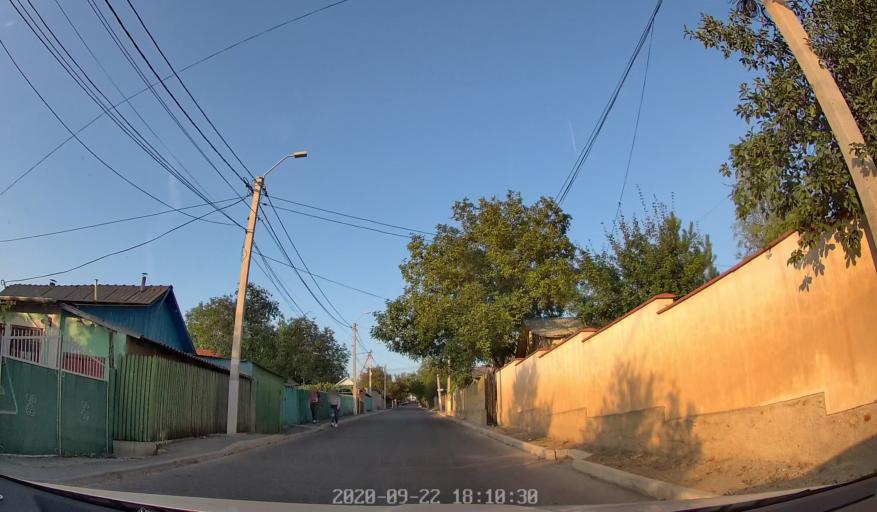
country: MD
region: Laloveni
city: Ialoveni
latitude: 46.9465
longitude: 28.7793
